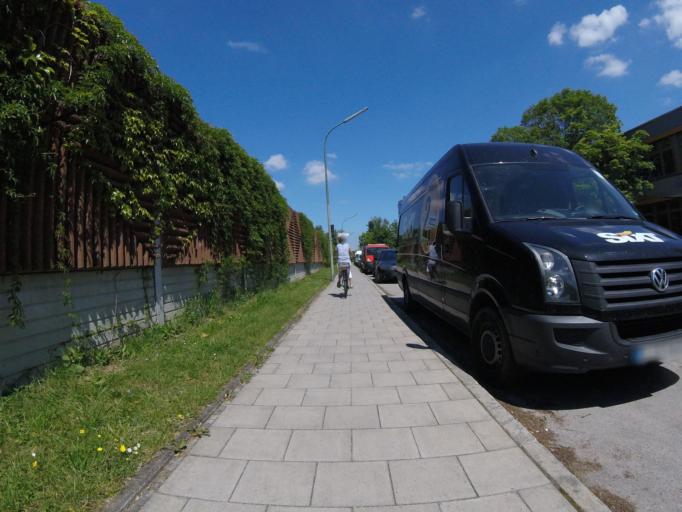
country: DE
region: Bavaria
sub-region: Upper Bavaria
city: Neubiberg
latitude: 48.0727
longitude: 11.6524
